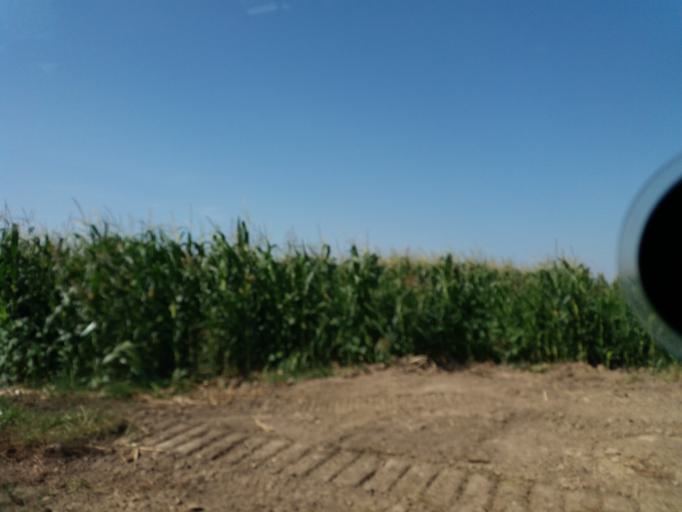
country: RS
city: Simanovci
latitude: 44.8928
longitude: 20.1008
